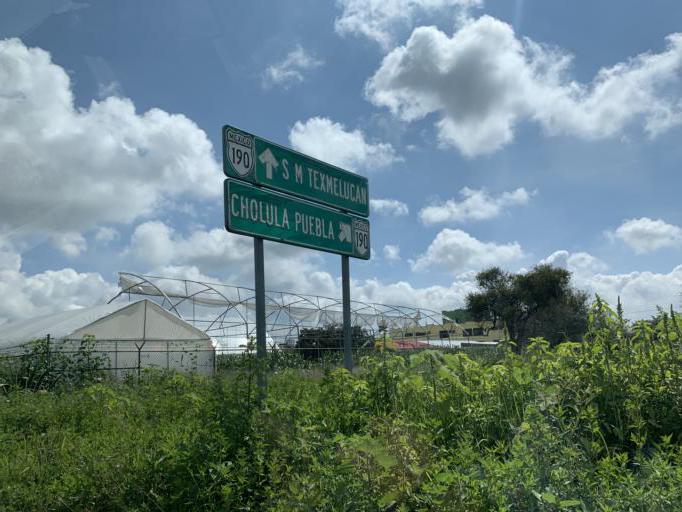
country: MX
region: Puebla
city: Huejotzingo
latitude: 19.1492
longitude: -98.4075
